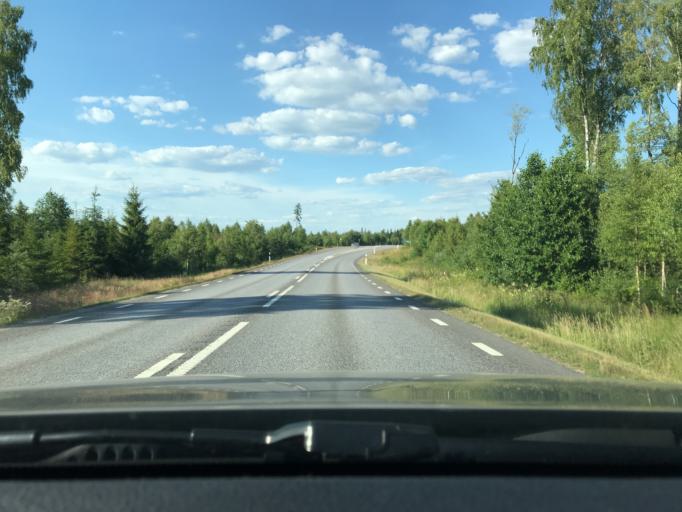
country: SE
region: Kronoberg
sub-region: Vaxjo Kommun
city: Gemla
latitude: 56.8268
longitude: 14.6922
